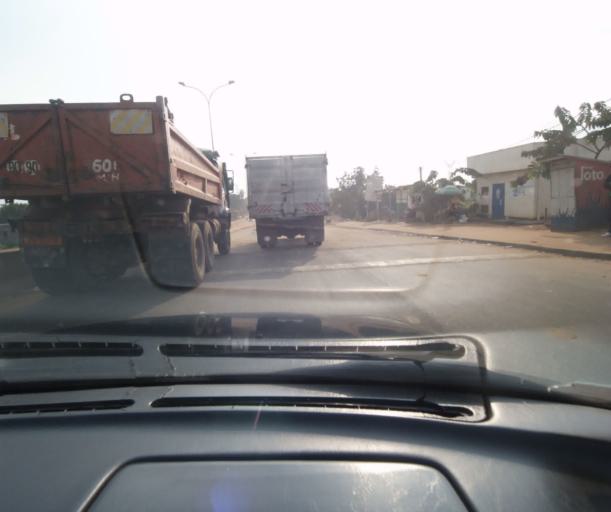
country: CM
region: Centre
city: Okoa
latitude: 3.9532
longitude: 11.5294
